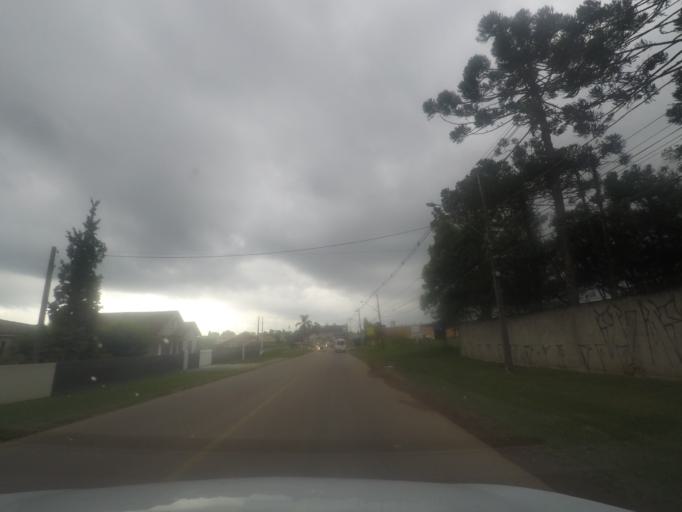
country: BR
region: Parana
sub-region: Sao Jose Dos Pinhais
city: Sao Jose dos Pinhais
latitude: -25.5611
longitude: -49.2684
